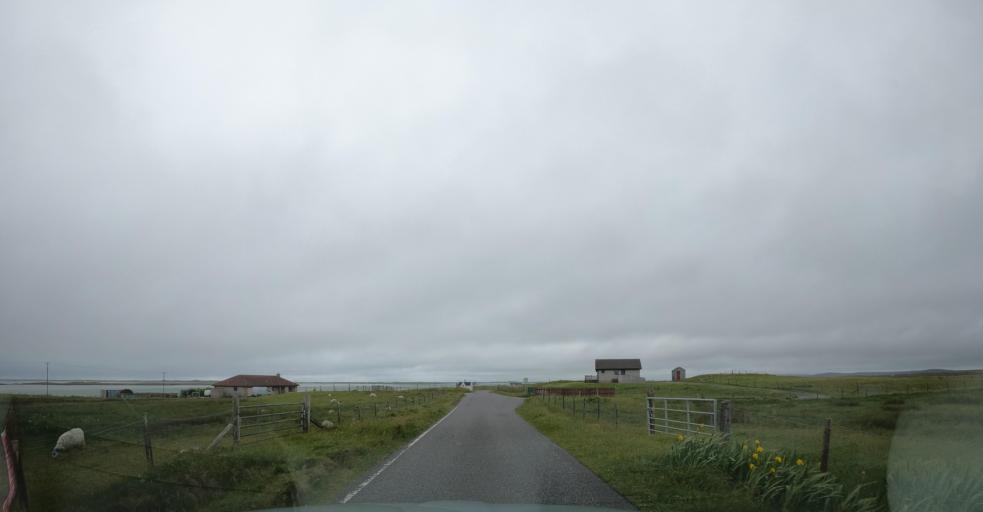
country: GB
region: Scotland
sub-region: Eilean Siar
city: Isle of North Uist
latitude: 57.5575
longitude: -7.3609
